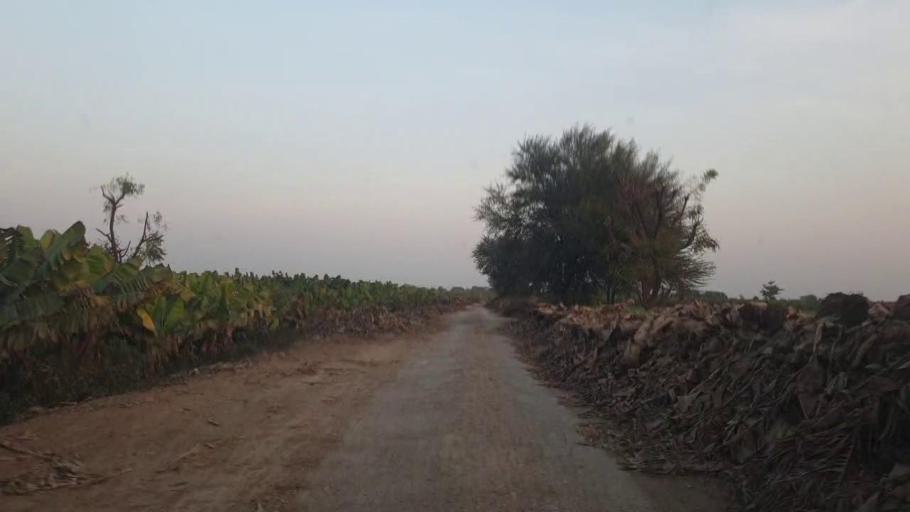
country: PK
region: Sindh
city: Bhit Shah
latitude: 25.8458
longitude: 68.5230
